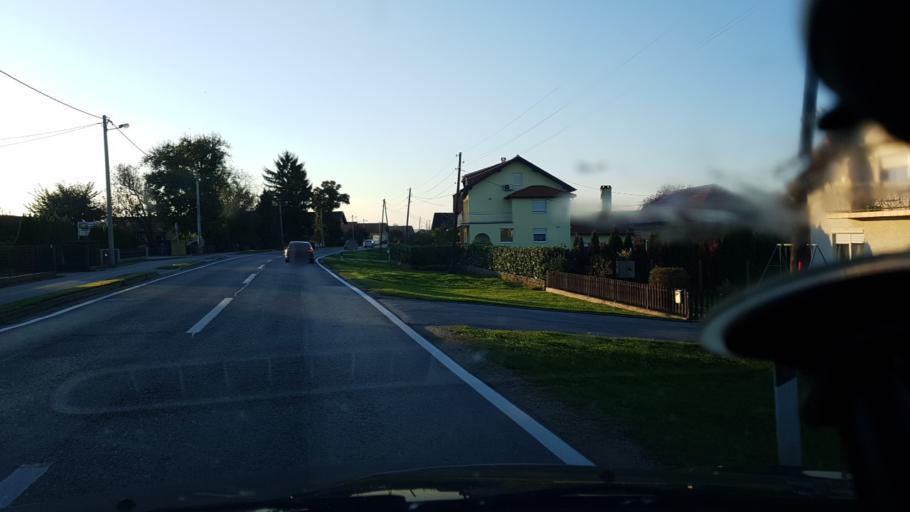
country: HR
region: Koprivnicko-Krizevacka
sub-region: Grad Koprivnica
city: Koprivnica
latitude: 46.1343
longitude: 16.8621
